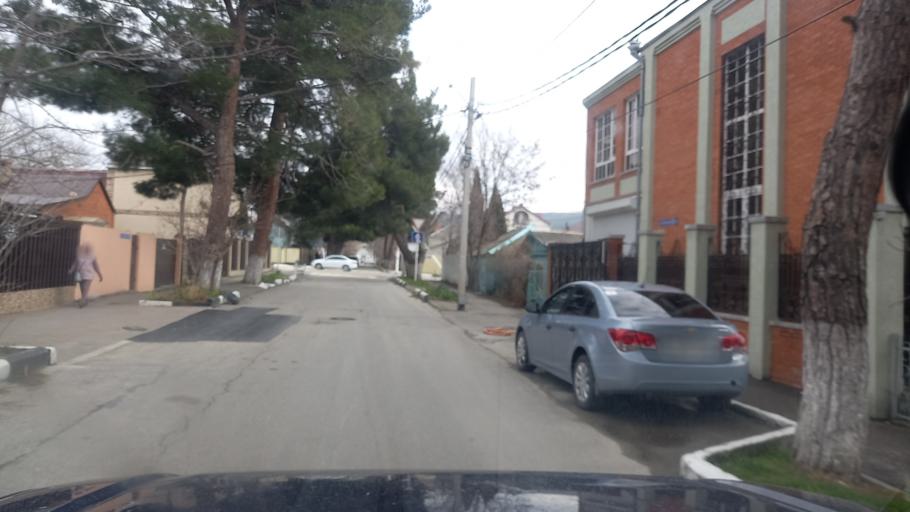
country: RU
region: Krasnodarskiy
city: Gelendzhik
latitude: 44.5597
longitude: 38.0867
